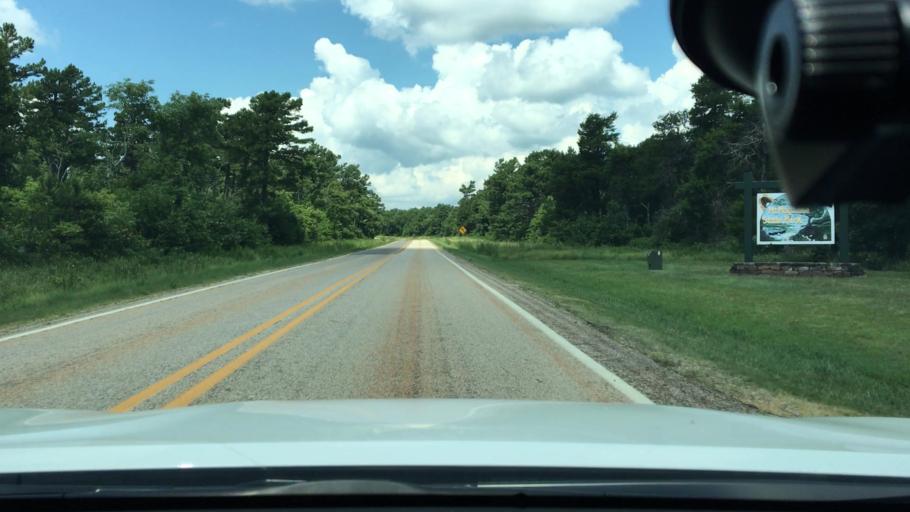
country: US
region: Arkansas
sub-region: Logan County
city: Paris
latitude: 35.1766
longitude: -93.5998
